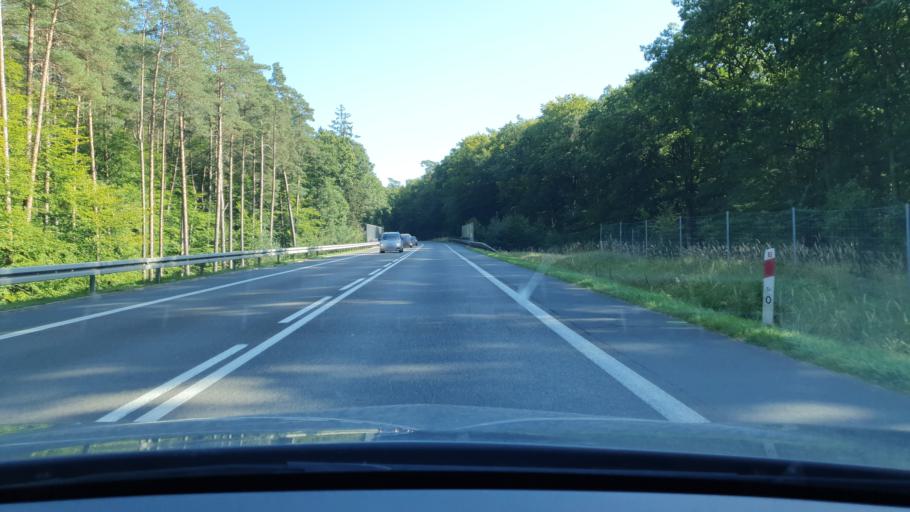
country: PL
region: West Pomeranian Voivodeship
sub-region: Powiat kamienski
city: Miedzyzdroje
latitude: 53.8978
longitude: 14.4666
